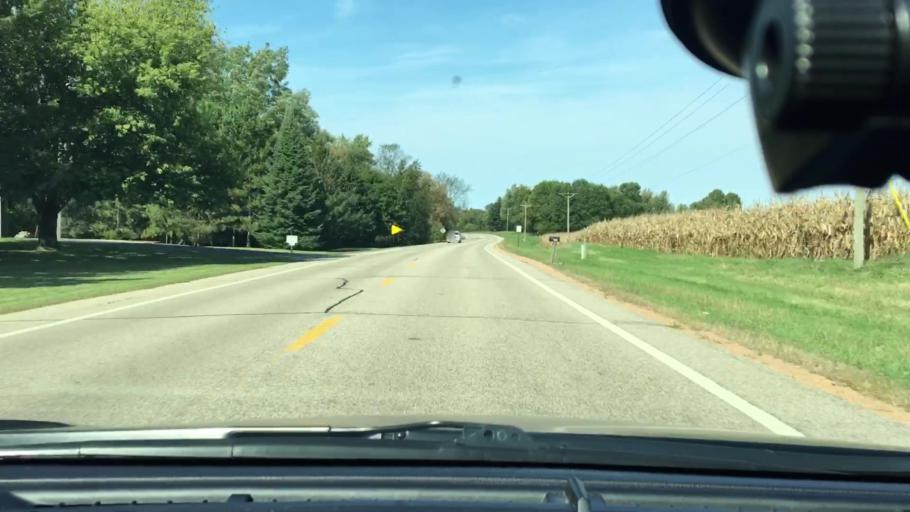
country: US
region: Minnesota
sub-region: Hennepin County
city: Corcoran
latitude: 45.0981
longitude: -93.5521
